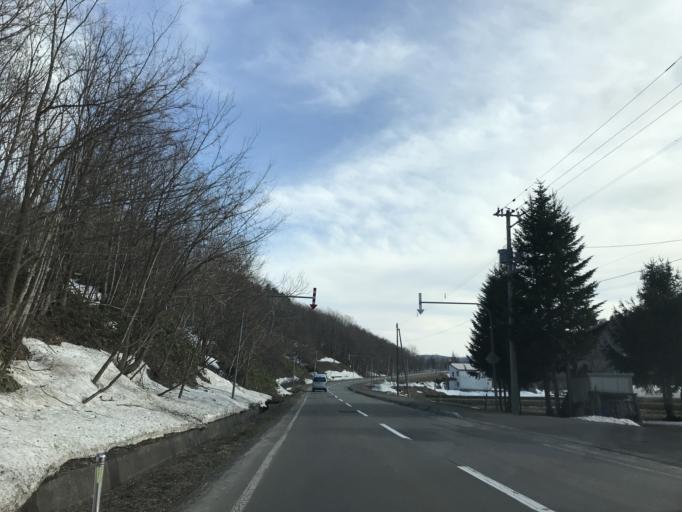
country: JP
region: Hokkaido
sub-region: Asahikawa-shi
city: Asahikawa
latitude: 43.7232
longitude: 142.3196
